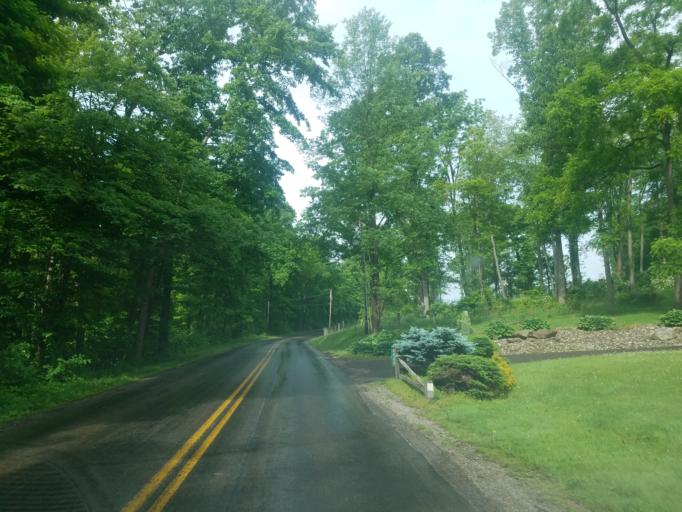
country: US
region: Ohio
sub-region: Holmes County
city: Millersburg
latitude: 40.5083
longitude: -81.8632
